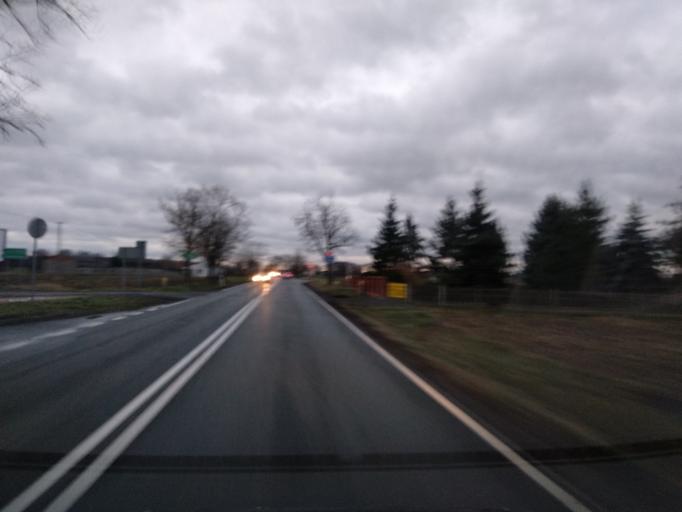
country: PL
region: Greater Poland Voivodeship
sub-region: Powiat koninski
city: Rychwal
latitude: 52.1033
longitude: 18.1672
